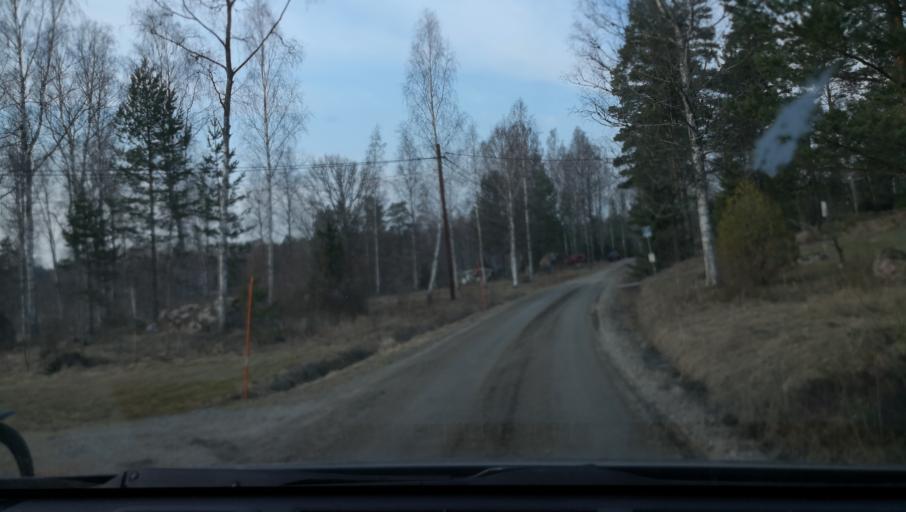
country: SE
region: OErebro
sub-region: Lindesbergs Kommun
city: Frovi
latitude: 59.3833
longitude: 15.3605
